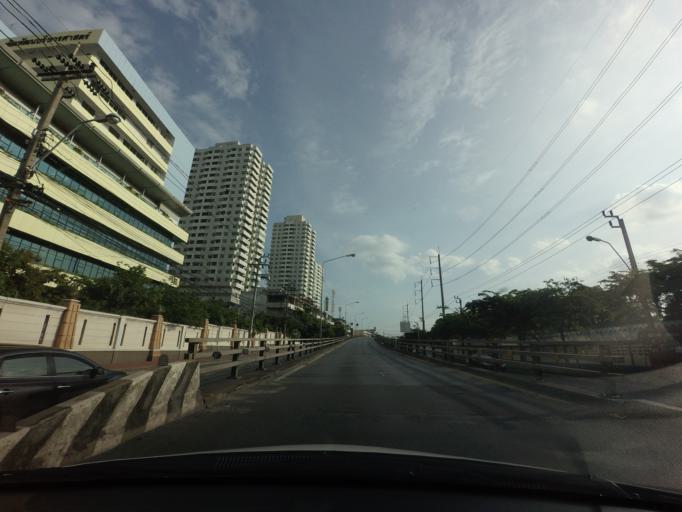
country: TH
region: Bangkok
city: Bang Kapi
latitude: 13.7693
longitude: 100.6520
